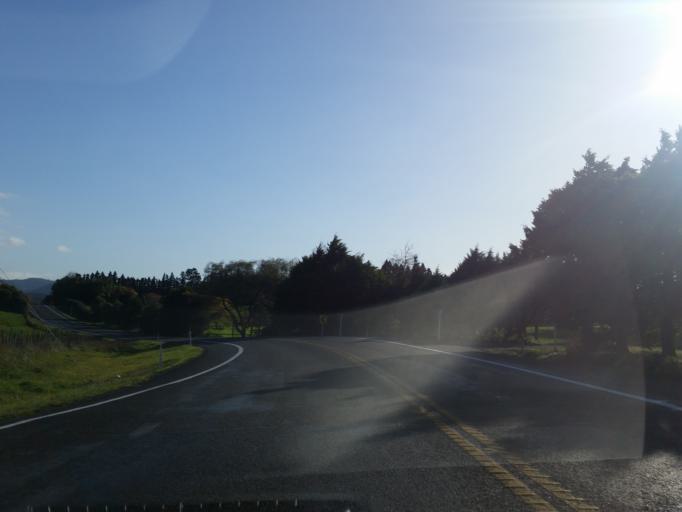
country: NZ
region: Waikato
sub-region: Hauraki District
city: Waihi
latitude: -37.4357
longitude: 175.8734
